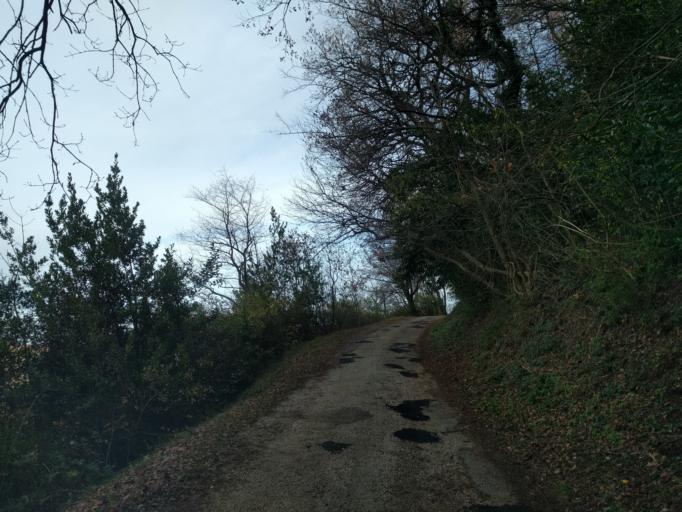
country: IT
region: The Marches
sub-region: Provincia di Pesaro e Urbino
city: Centinarola
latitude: 43.8186
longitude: 12.9732
